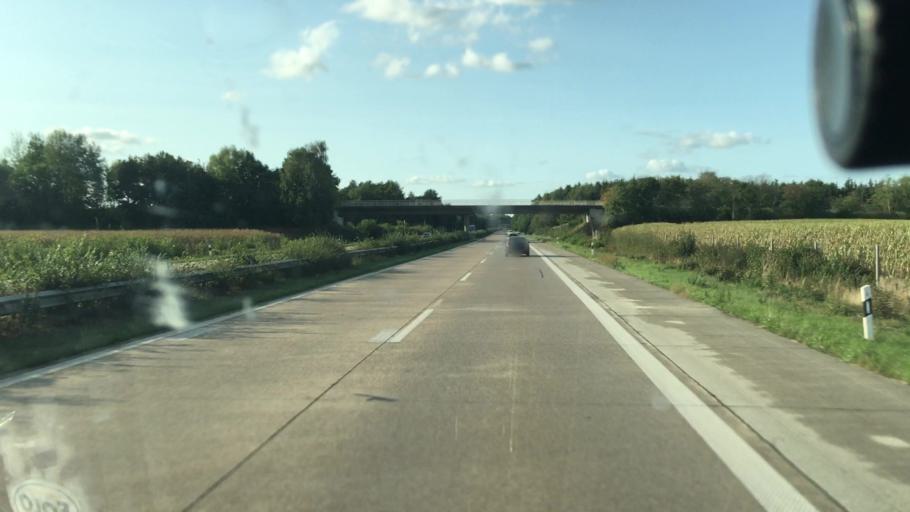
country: DE
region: Lower Saxony
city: Rastede
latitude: 53.2592
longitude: 8.1692
